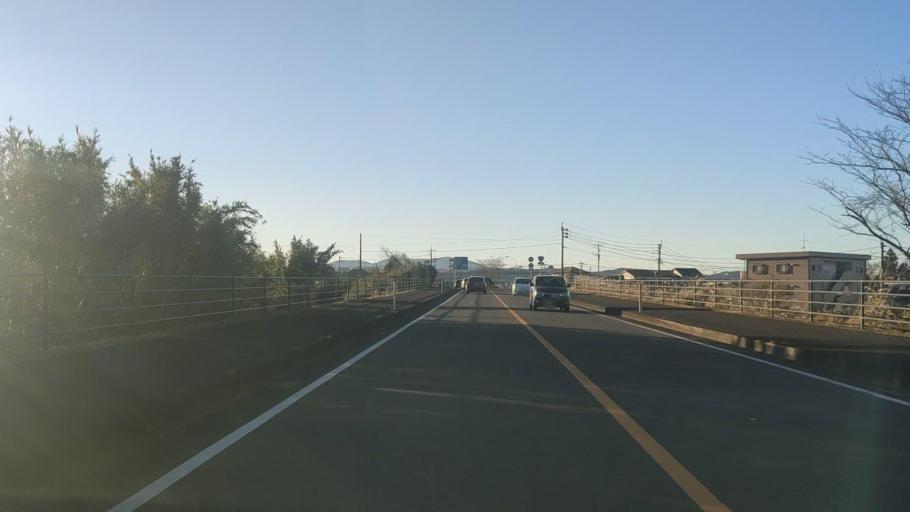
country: JP
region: Miyazaki
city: Miyazaki-shi
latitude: 31.8315
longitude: 131.3025
